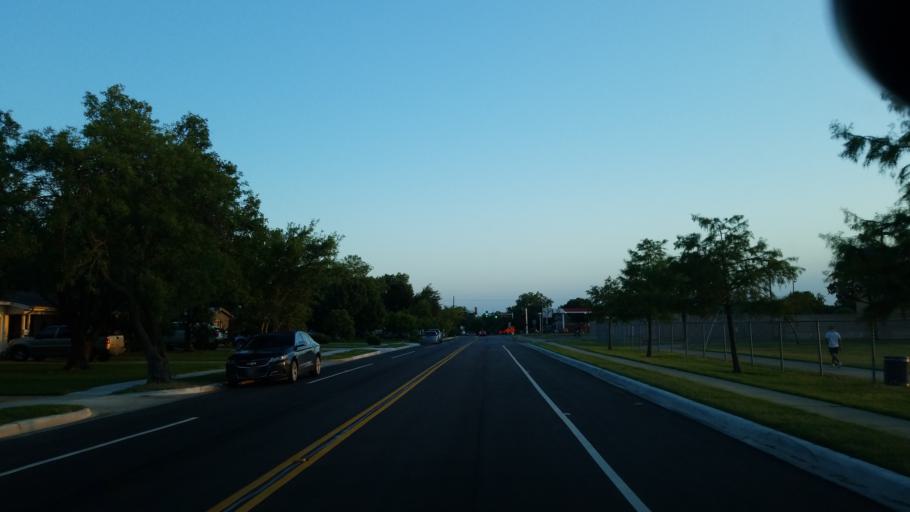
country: US
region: Texas
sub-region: Dallas County
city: Farmers Branch
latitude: 32.9350
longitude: -96.8868
